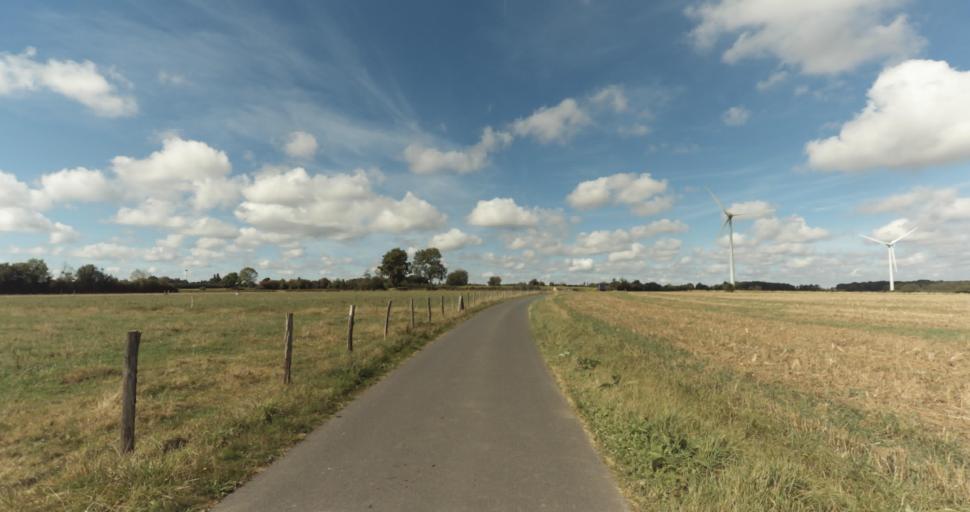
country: FR
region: Lower Normandy
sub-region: Departement du Calvados
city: Orbec
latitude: 48.9601
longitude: 0.3724
